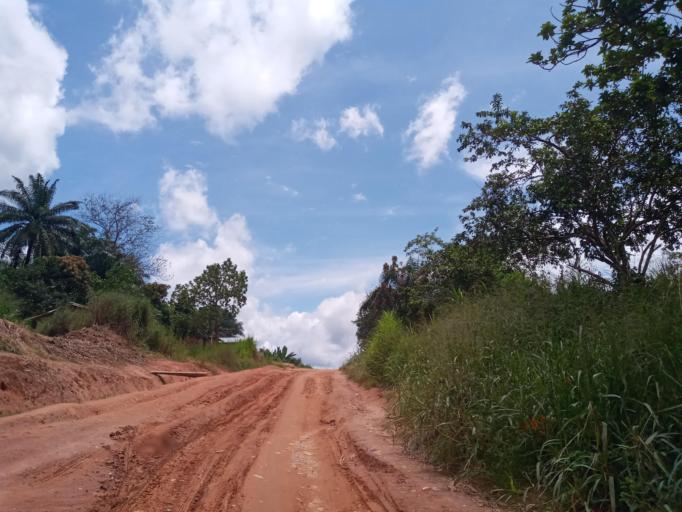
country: SL
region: Eastern Province
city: Koidu
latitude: 8.6449
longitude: -10.9171
